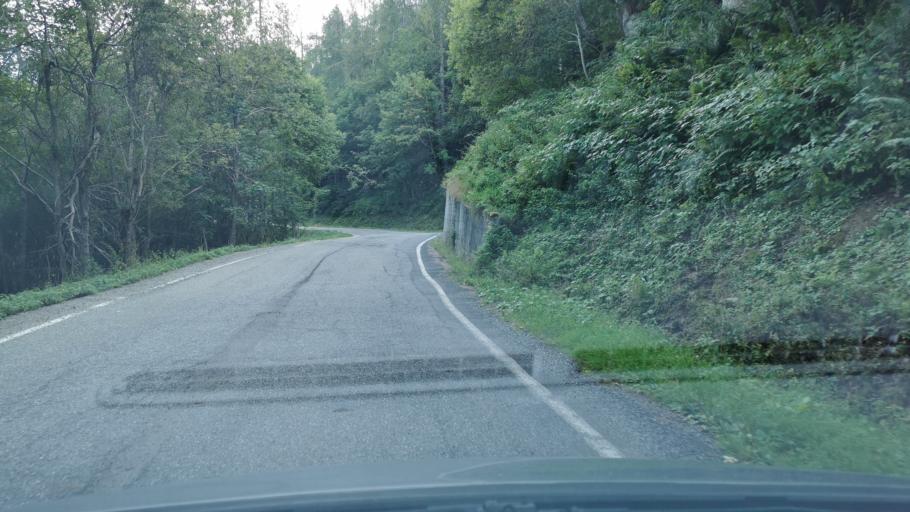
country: IT
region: Piedmont
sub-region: Provincia di Torino
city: Usseglio
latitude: 45.2249
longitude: 7.2173
